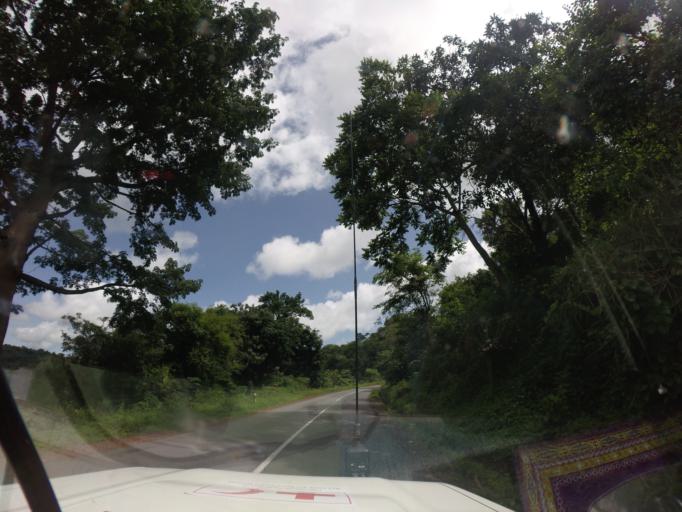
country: GN
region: Mamou
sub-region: Mamou Prefecture
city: Mamou
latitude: 10.2962
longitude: -11.9586
